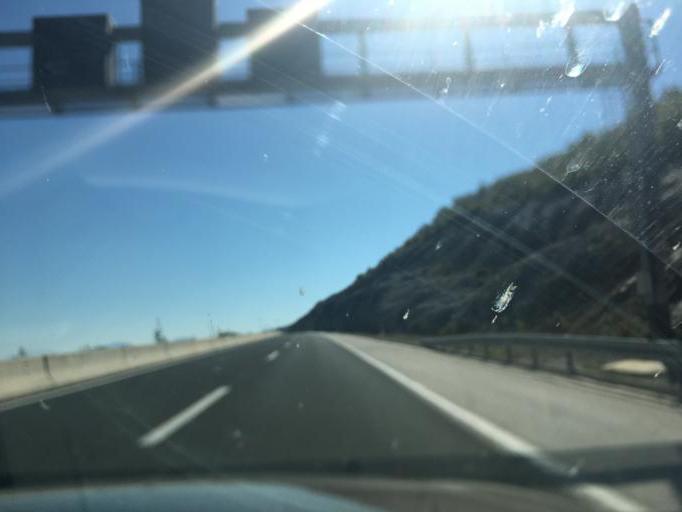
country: HR
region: Splitsko-Dalmatinska
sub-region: Grad Trogir
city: Trogir
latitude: 43.6283
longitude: 16.2327
